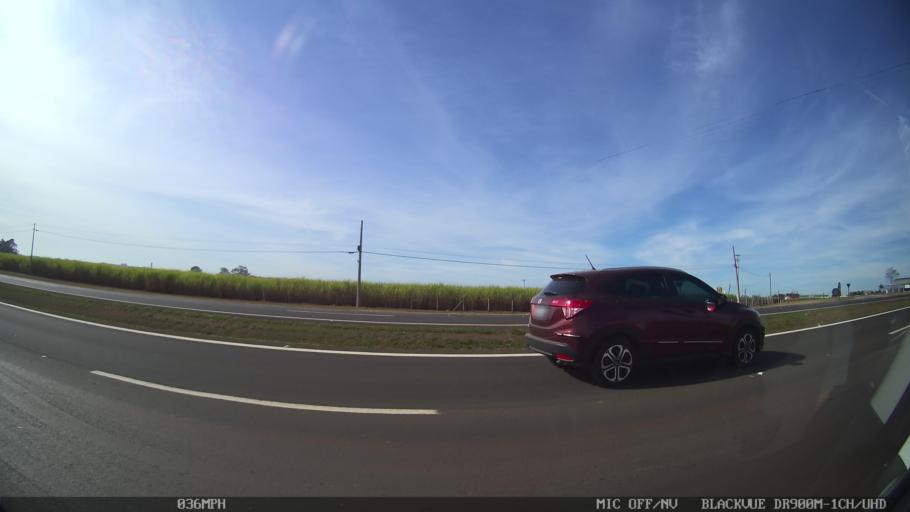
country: BR
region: Sao Paulo
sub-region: Piracicaba
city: Piracicaba
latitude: -22.7795
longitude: -47.6519
